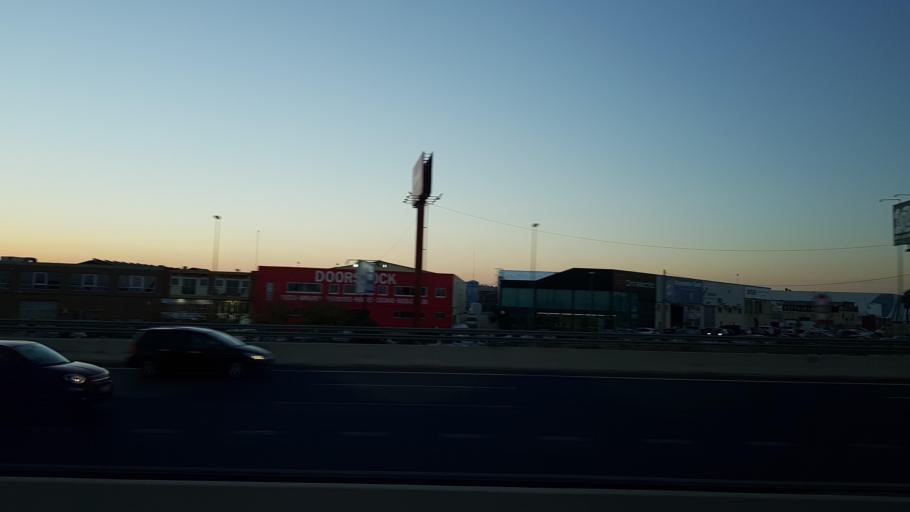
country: ES
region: Valencia
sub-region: Provincia de Valencia
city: Manises
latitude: 39.4805
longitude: -0.4657
